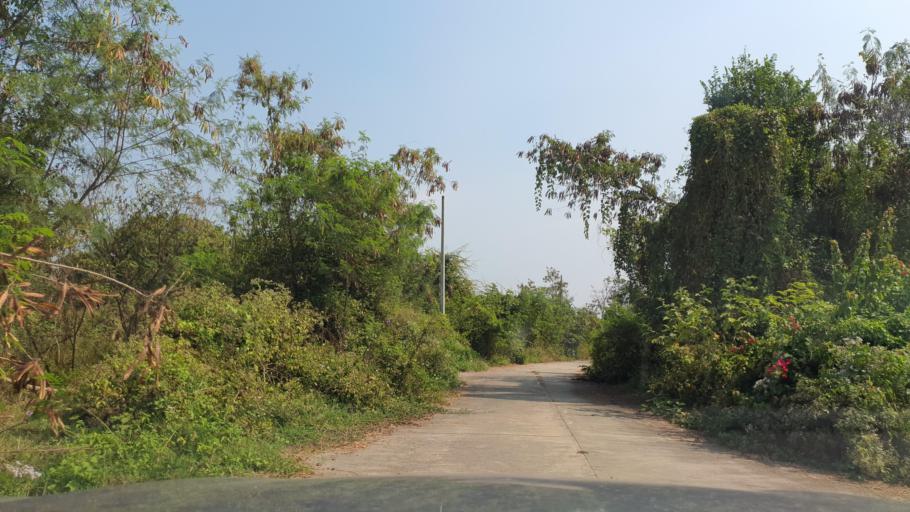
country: TH
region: Chiang Mai
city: San Pa Tong
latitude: 18.6532
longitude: 98.8893
